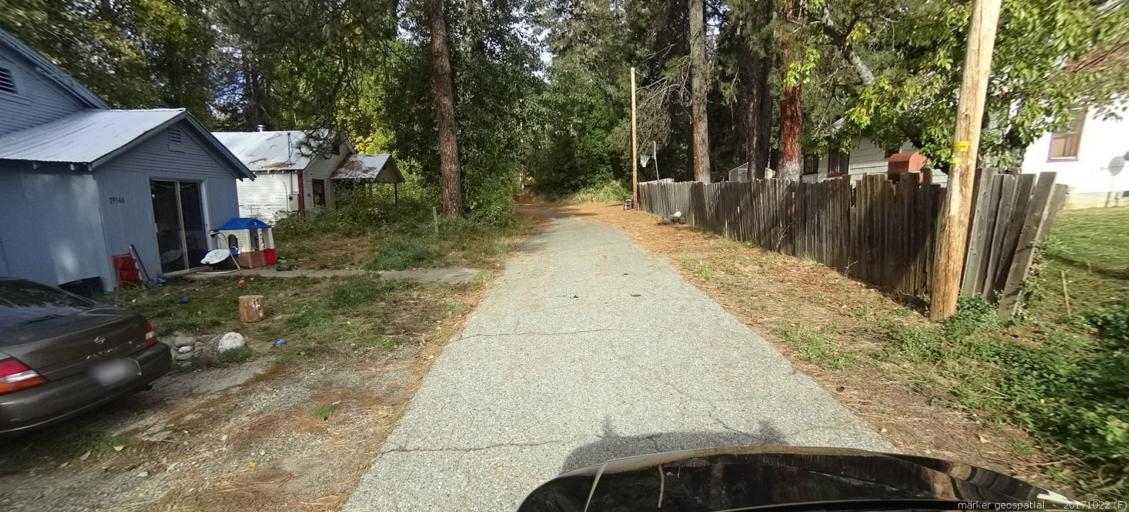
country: US
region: California
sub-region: Siskiyou County
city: Dunsmuir
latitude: 41.1469
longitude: -122.3209
